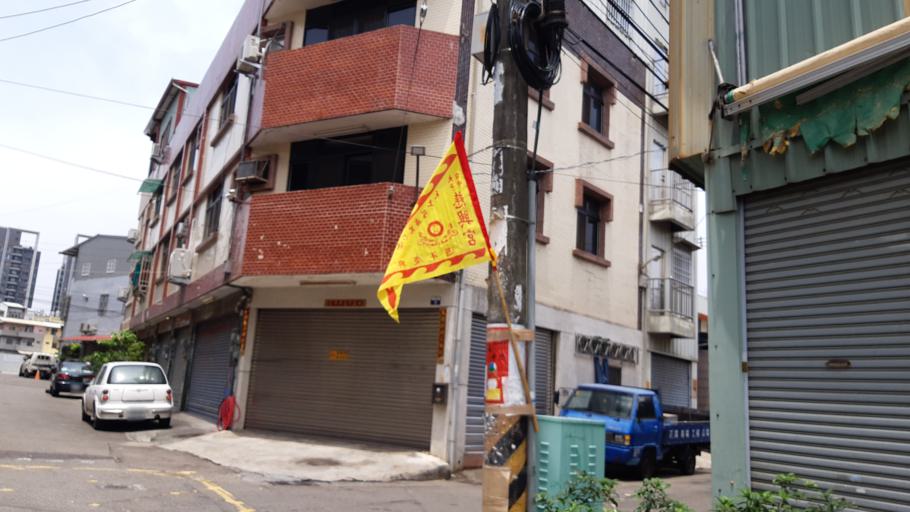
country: TW
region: Taiwan
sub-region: Taichung City
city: Taichung
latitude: 24.1540
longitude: 120.7302
